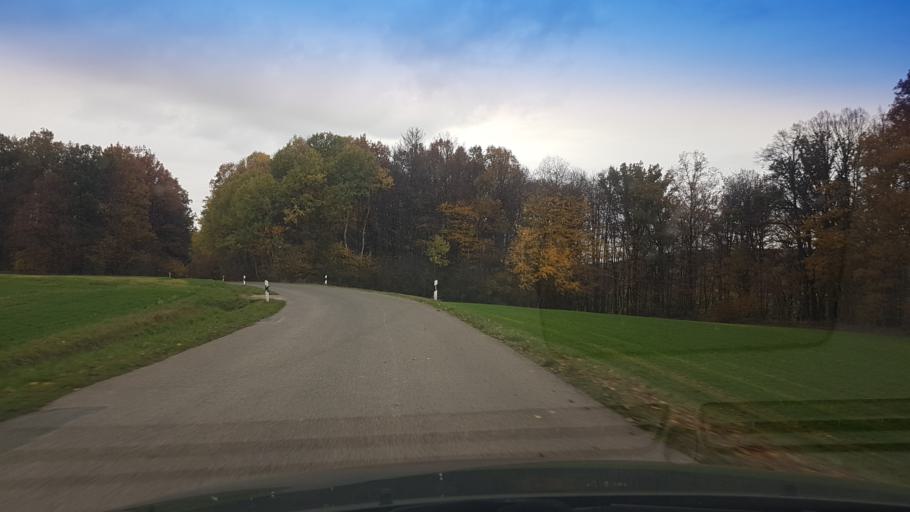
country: DE
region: Bavaria
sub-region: Upper Franconia
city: Rattelsdorf
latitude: 50.0383
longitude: 10.8780
